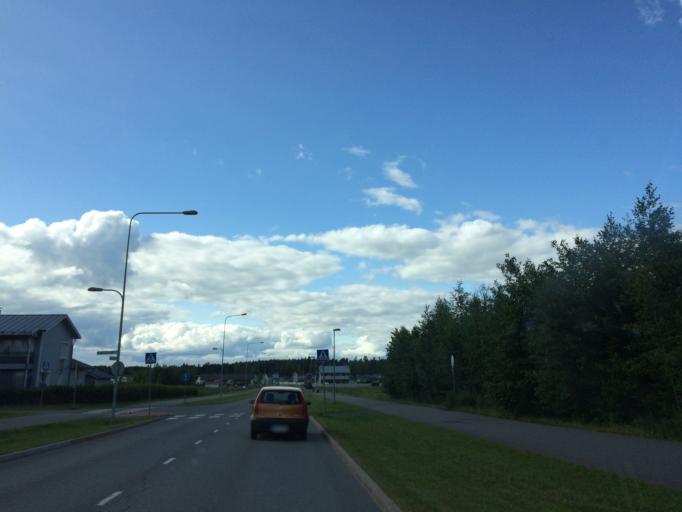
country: FI
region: Haeme
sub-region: Haemeenlinna
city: Parola
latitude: 60.9738
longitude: 24.3807
